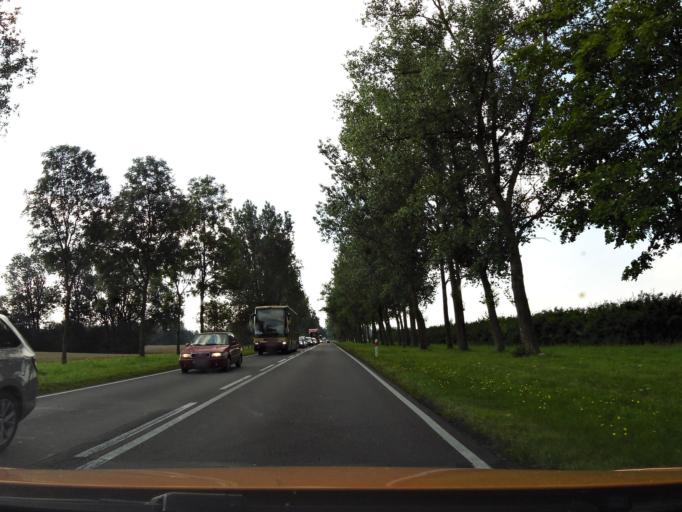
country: PL
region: West Pomeranian Voivodeship
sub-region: Powiat gryficki
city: Ploty
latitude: 53.7846
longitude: 15.2500
